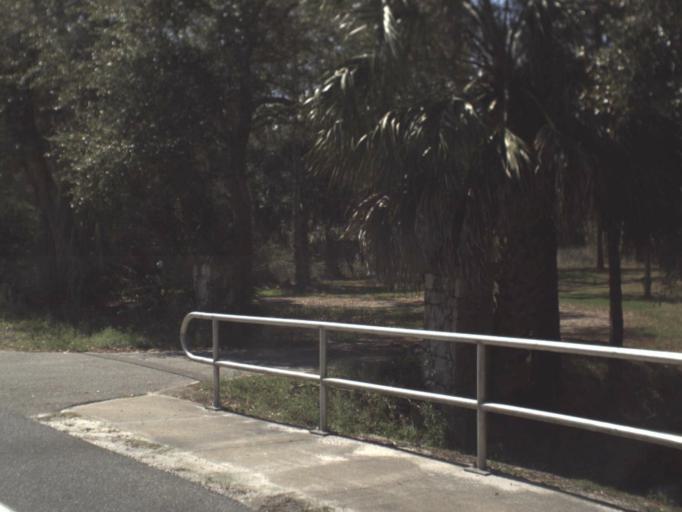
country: US
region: Florida
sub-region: Wakulla County
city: Crawfordville
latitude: 30.0347
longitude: -84.3894
